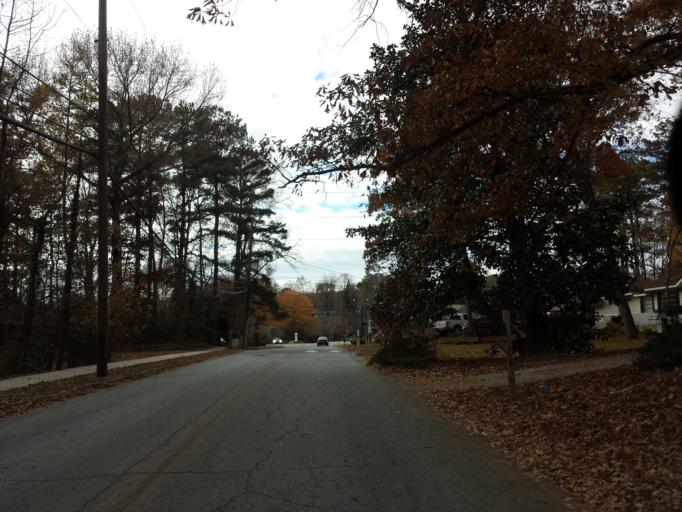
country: US
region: Georgia
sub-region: DeKalb County
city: Dunwoody
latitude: 33.9363
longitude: -84.3366
